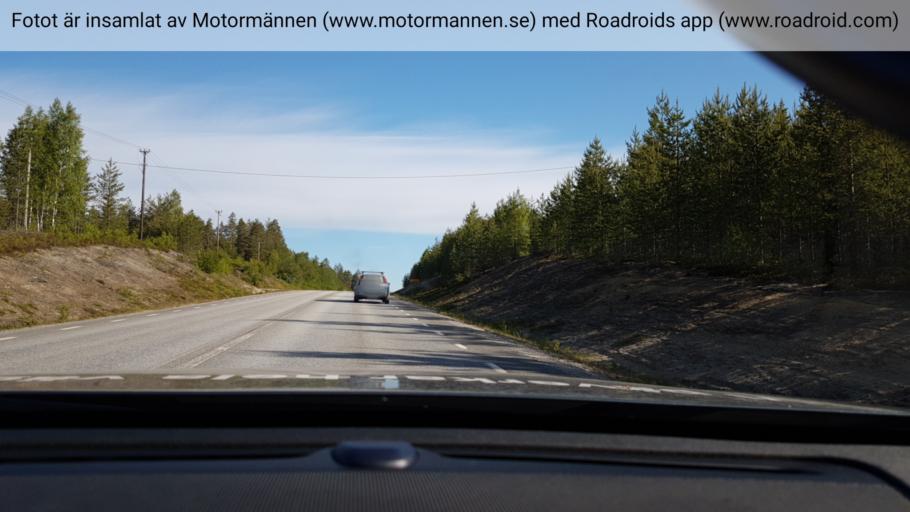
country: SE
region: Vaesterbotten
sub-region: Vannas Kommun
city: Vaennaes
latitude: 64.0293
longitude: 19.6924
